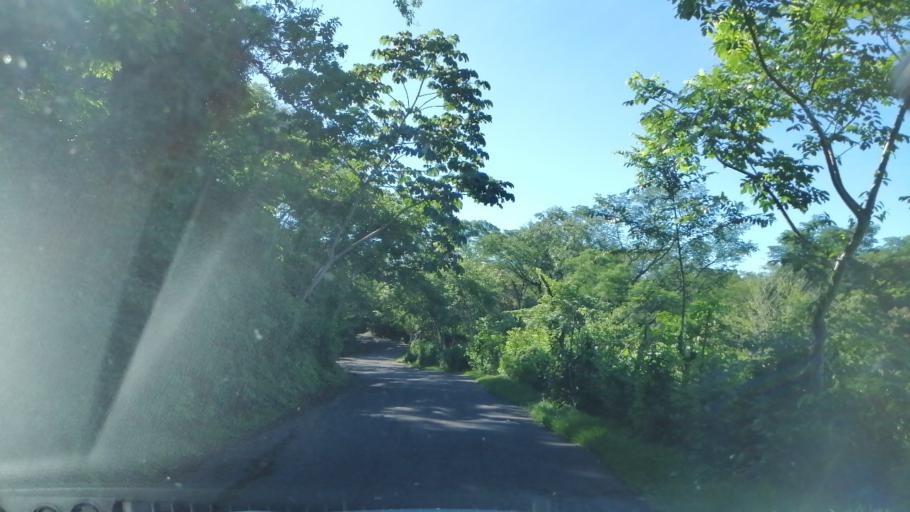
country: SV
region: Morazan
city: Corinto
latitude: 13.7908
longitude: -88.0209
